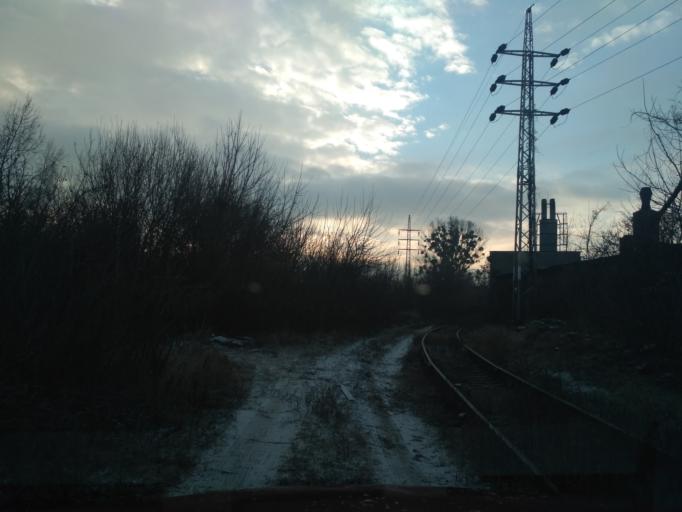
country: SK
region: Kosicky
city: Kosice
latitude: 48.7295
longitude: 21.2678
